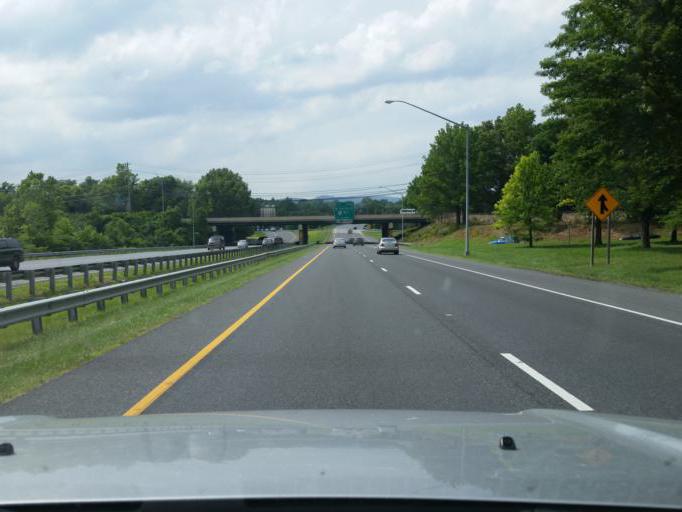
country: US
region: Maryland
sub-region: Frederick County
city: Frederick
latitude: 39.4046
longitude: -77.4313
